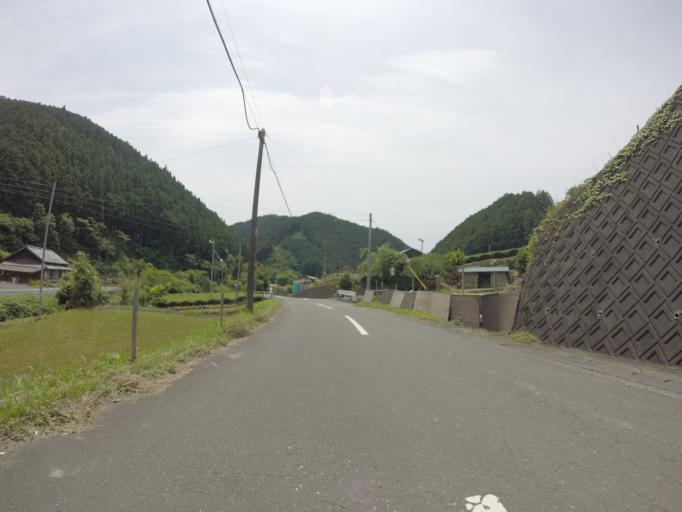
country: JP
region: Shizuoka
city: Shizuoka-shi
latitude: 35.0415
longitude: 138.2958
